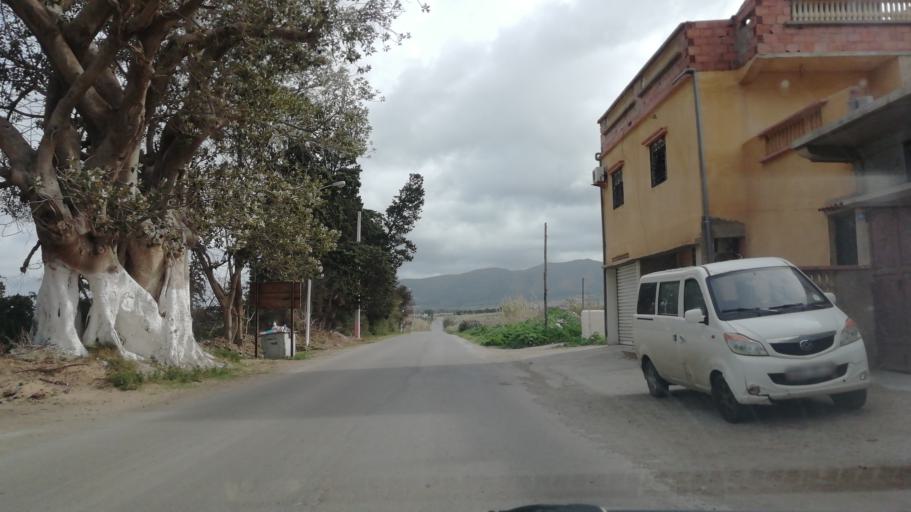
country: DZ
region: Oran
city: Bou Tlelis
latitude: 35.7009
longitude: -0.8911
